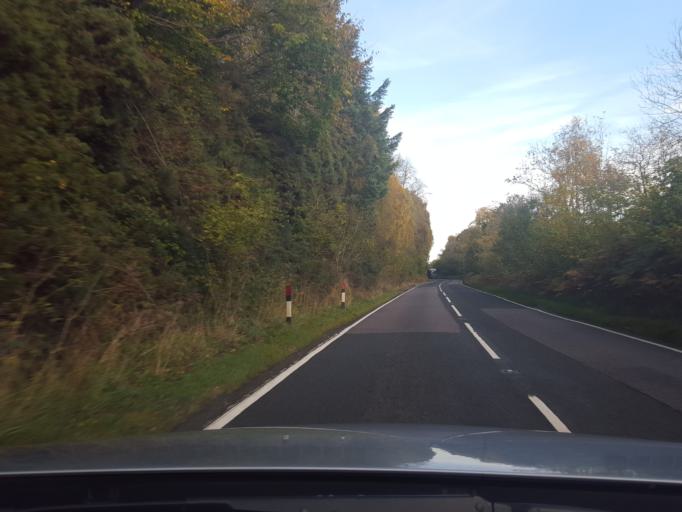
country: GB
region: Scotland
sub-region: Highland
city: Beauly
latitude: 57.3119
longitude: -4.4585
